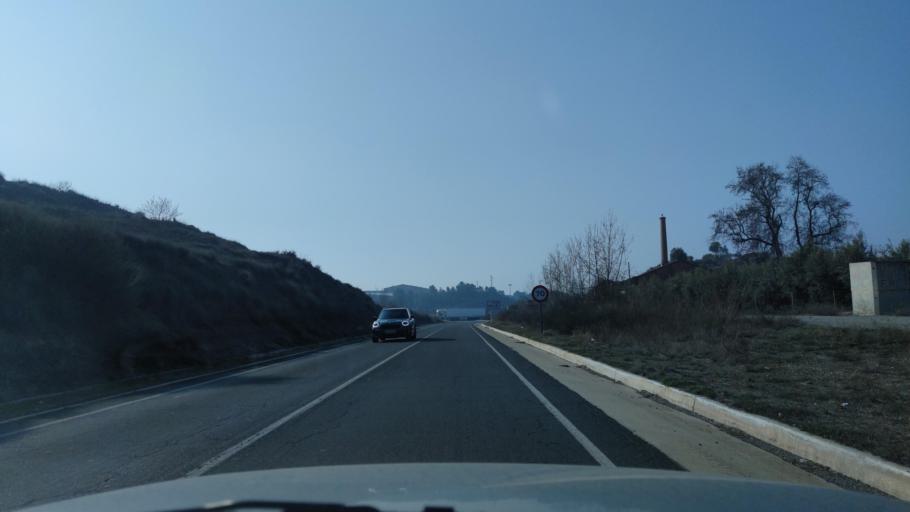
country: ES
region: Catalonia
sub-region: Provincia de Lleida
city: Sunyer
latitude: 41.5650
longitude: 0.5887
